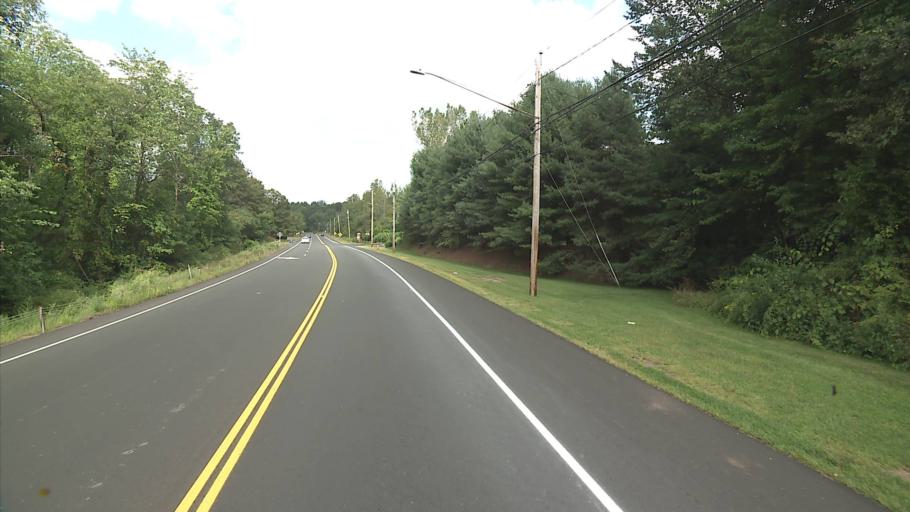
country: US
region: Connecticut
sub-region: Hartford County
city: Weatogue
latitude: 41.8417
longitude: -72.7906
